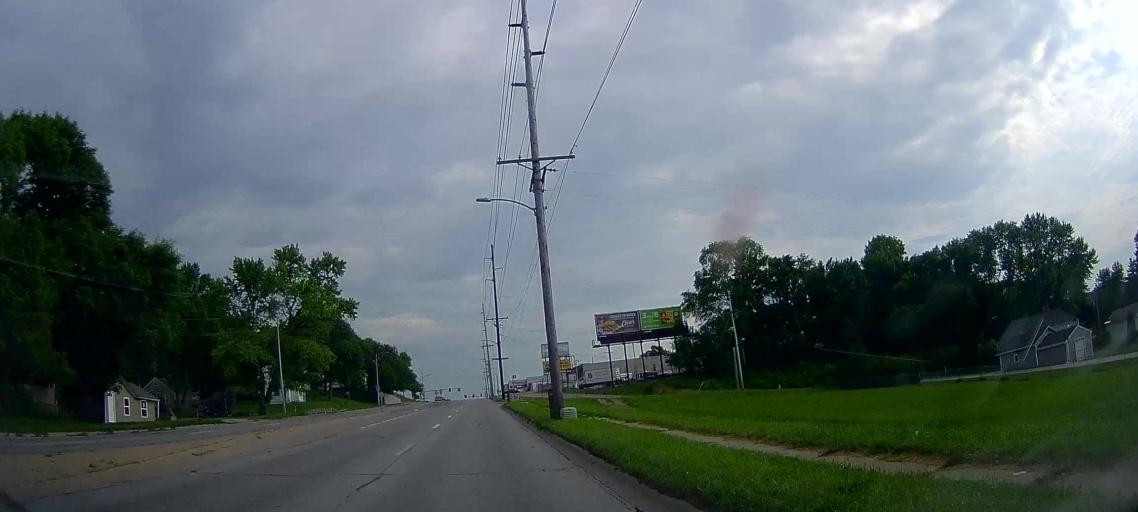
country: US
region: Nebraska
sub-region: Douglas County
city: Ralston
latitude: 41.2873
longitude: -96.0240
